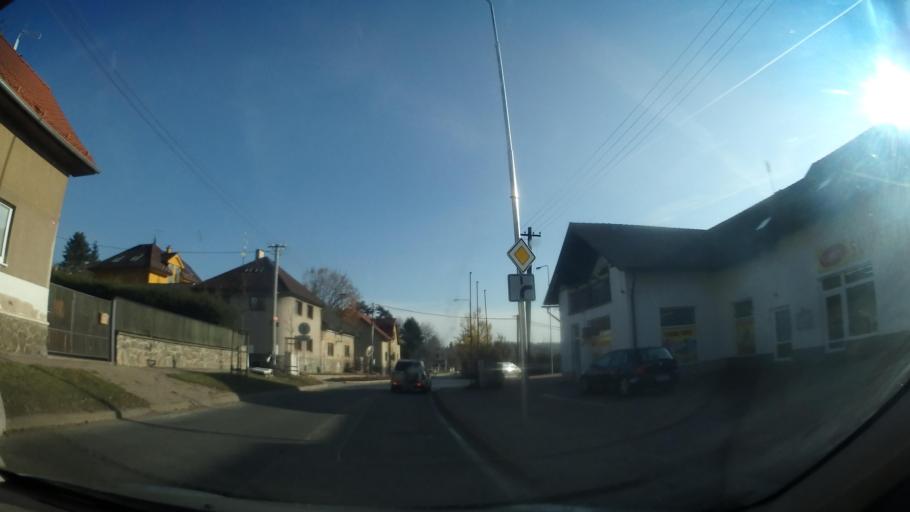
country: CZ
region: Central Bohemia
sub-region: Okres Praha-Vychod
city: Mnichovice
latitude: 49.9321
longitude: 14.7140
